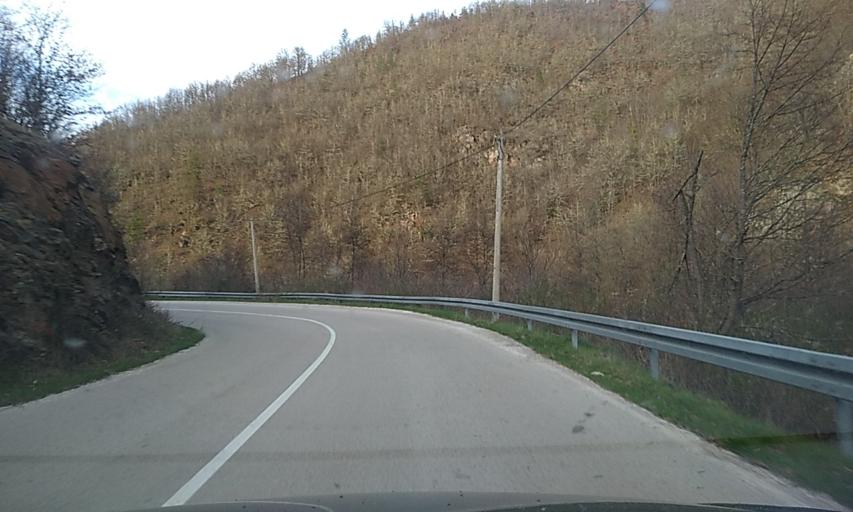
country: RS
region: Central Serbia
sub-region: Pcinjski Okrug
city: Bosilegrad
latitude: 42.4358
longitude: 22.5141
